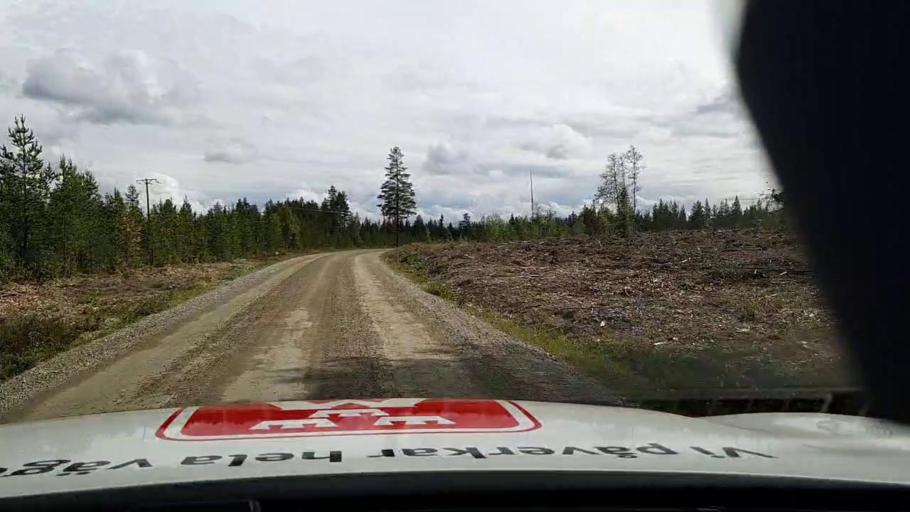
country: SE
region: Jaemtland
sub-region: Are Kommun
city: Jarpen
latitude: 62.5033
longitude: 13.5008
